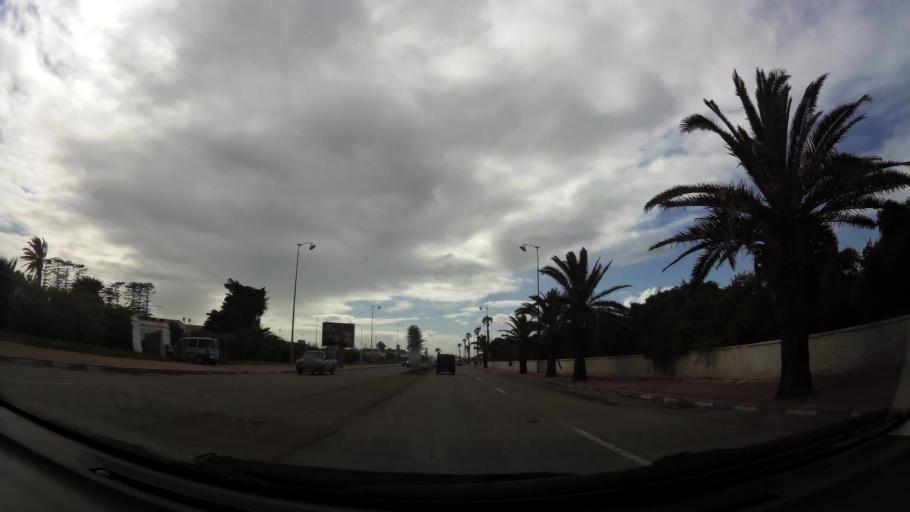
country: MA
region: Doukkala-Abda
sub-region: El-Jadida
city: El Jadida
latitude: 33.2438
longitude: -8.4741
